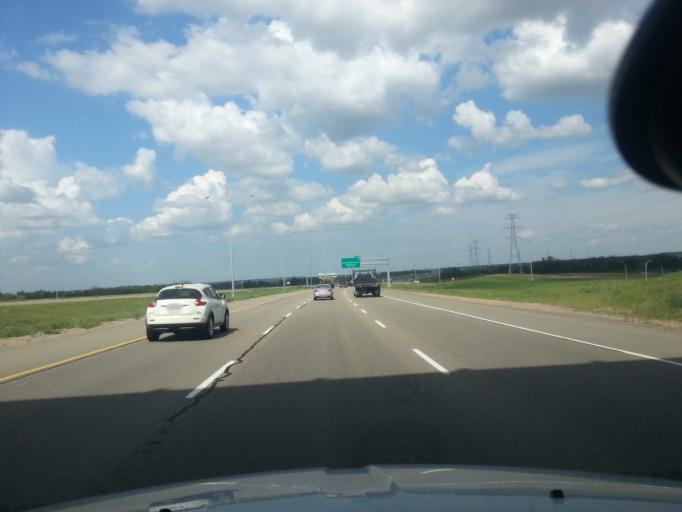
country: CA
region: Alberta
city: St. Albert
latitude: 53.5762
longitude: -113.6609
